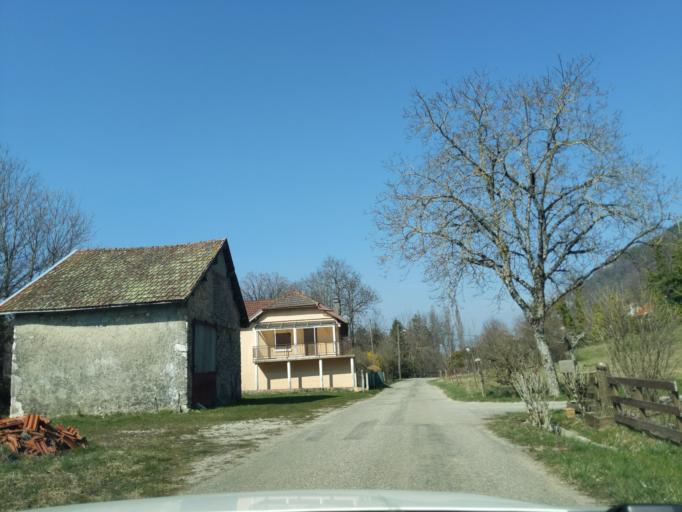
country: FR
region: Rhone-Alpes
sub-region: Departement de la Haute-Savoie
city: Moye
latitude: 45.9088
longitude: 5.8495
